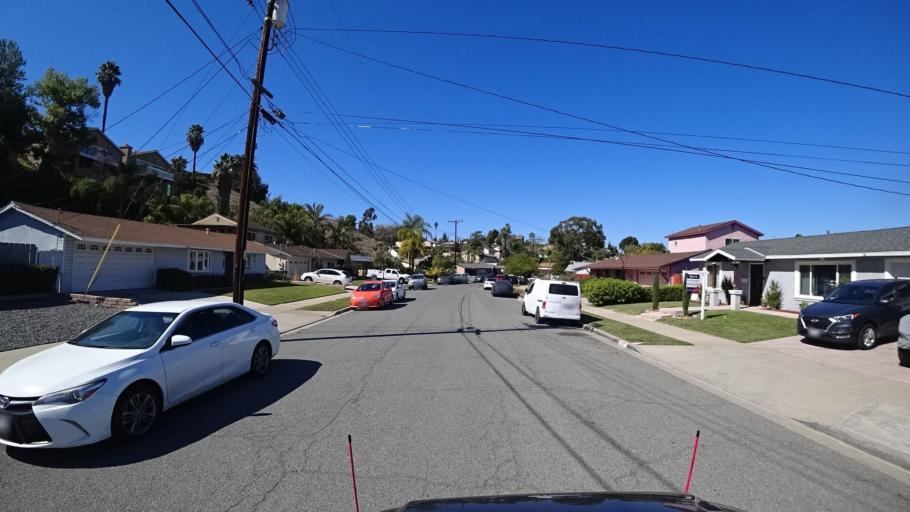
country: US
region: California
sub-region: San Diego County
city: La Presa
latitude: 32.7156
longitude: -117.0222
